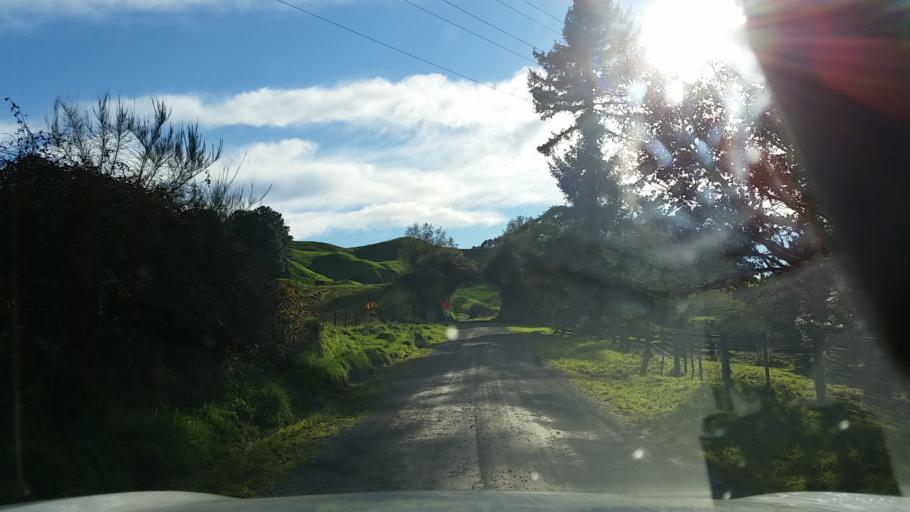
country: NZ
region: Waikato
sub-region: South Waikato District
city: Tokoroa
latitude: -38.3661
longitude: 176.0886
